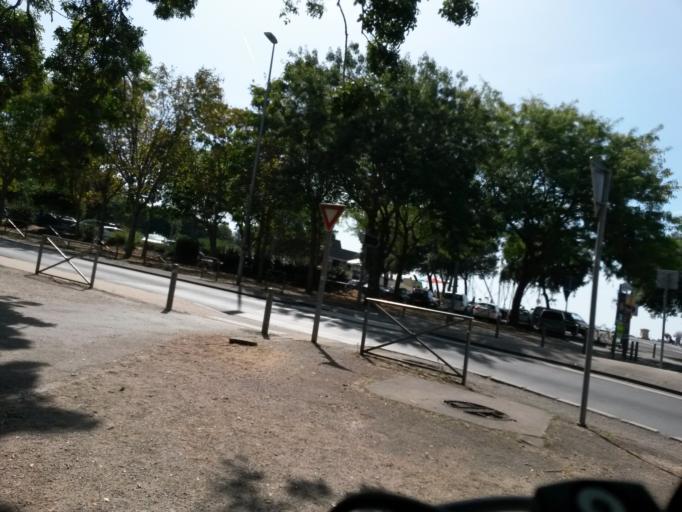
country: FR
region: Poitou-Charentes
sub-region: Departement de la Charente-Maritime
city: La Rochelle
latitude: 46.1562
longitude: -1.1608
